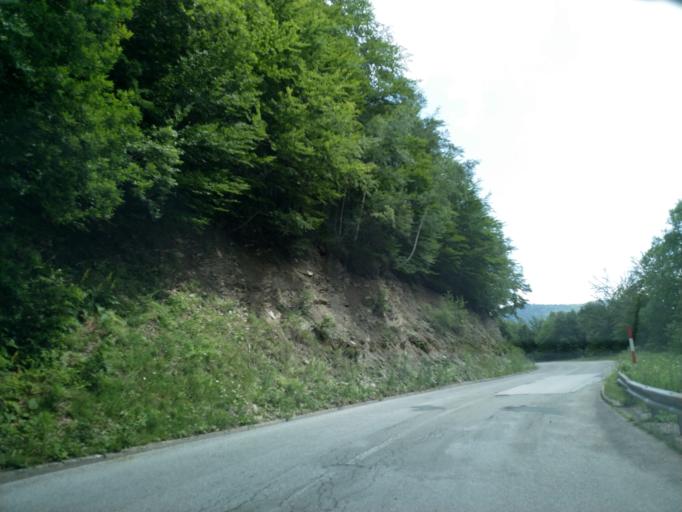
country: XK
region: Mitrovica
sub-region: Komuna e Leposaviqit
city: Leposaviq
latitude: 43.3106
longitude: 20.8602
